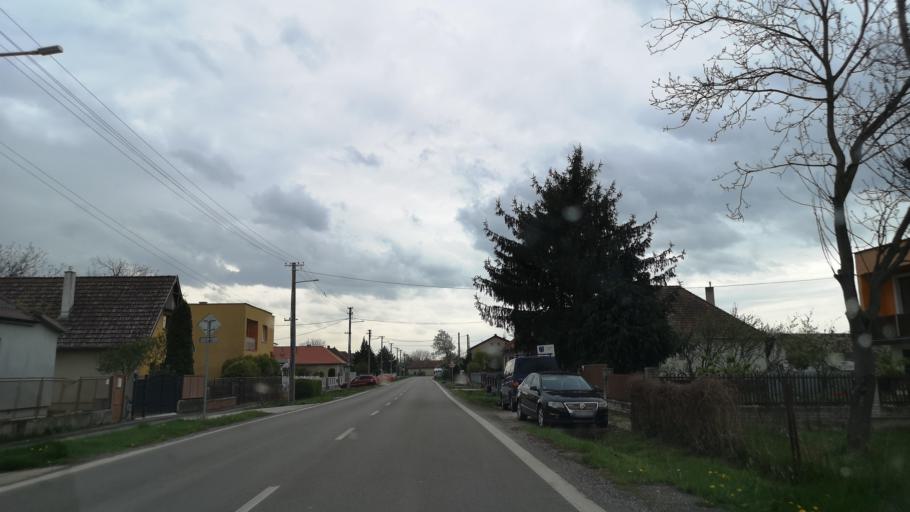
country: SK
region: Nitriansky
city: Zlate Moravce
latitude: 48.3484
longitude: 18.3661
